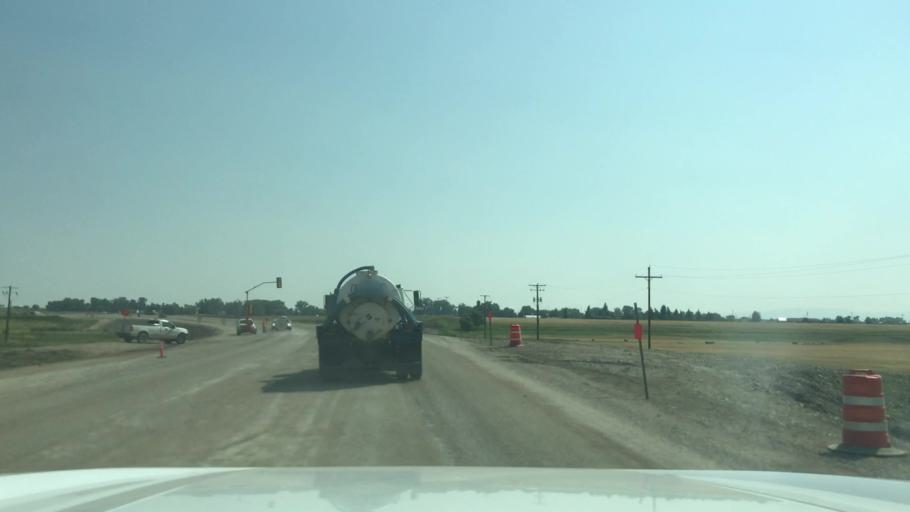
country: US
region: Montana
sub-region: Judith Basin County
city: Stanford
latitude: 47.0103
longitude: -109.8723
